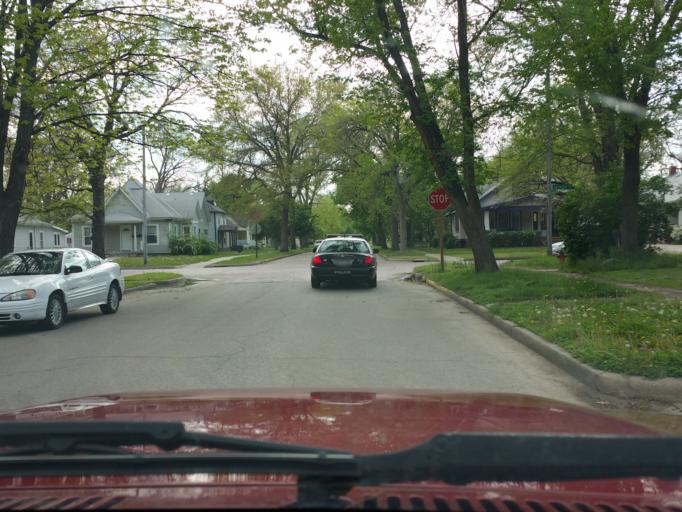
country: US
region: Kansas
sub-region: Riley County
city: Manhattan
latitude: 39.1847
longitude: -96.5661
